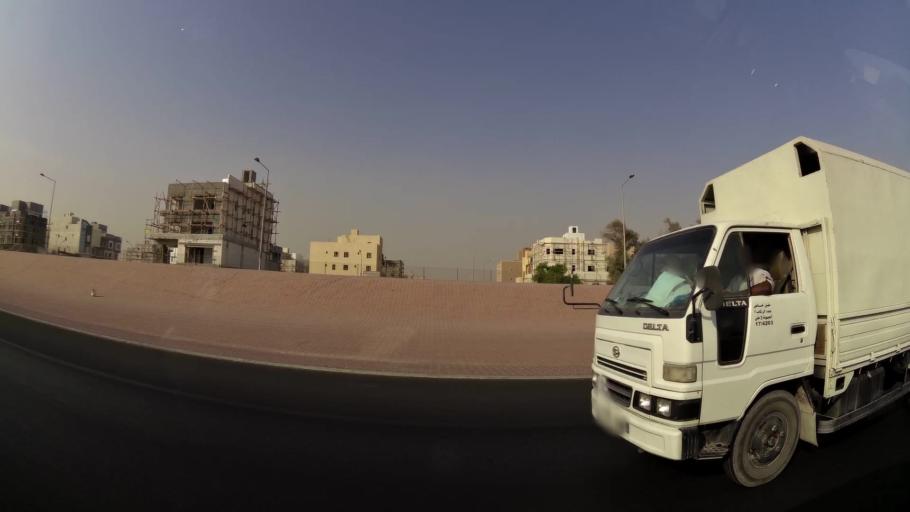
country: KW
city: Al Funaytis
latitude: 29.2317
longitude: 48.0972
